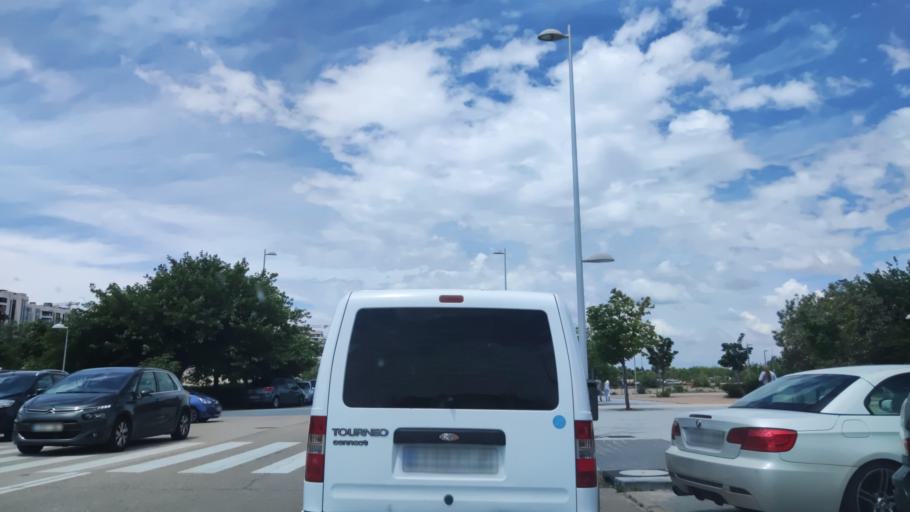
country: ES
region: Madrid
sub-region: Provincia de Madrid
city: Barajas de Madrid
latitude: 40.4858
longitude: -3.6065
